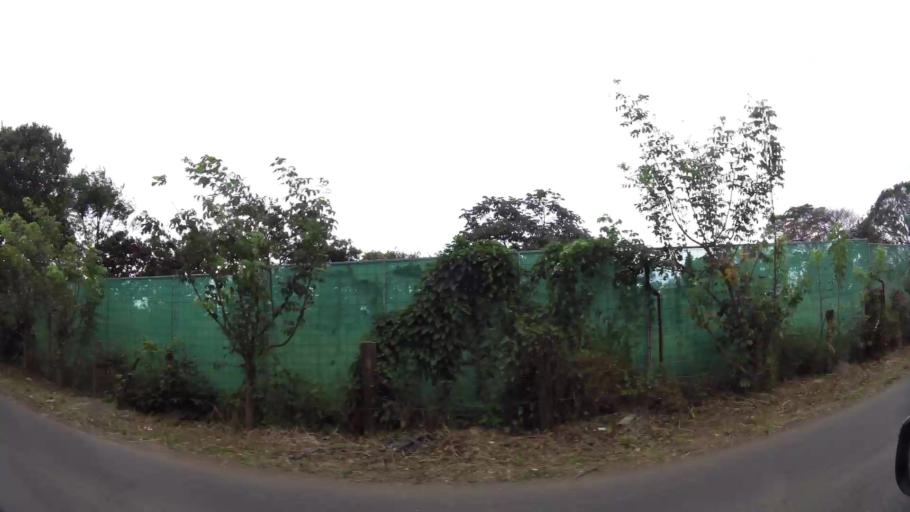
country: CR
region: Heredia
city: La Asuncion
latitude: 9.9649
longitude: -84.1823
